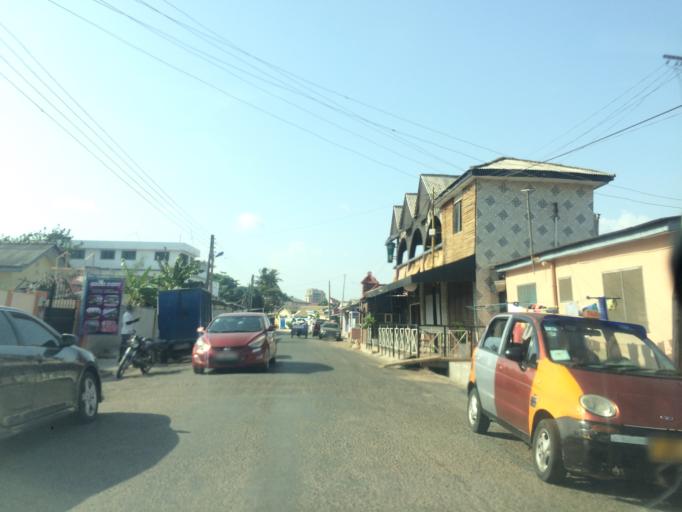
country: GH
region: Greater Accra
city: Accra
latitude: 5.5570
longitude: -0.1771
